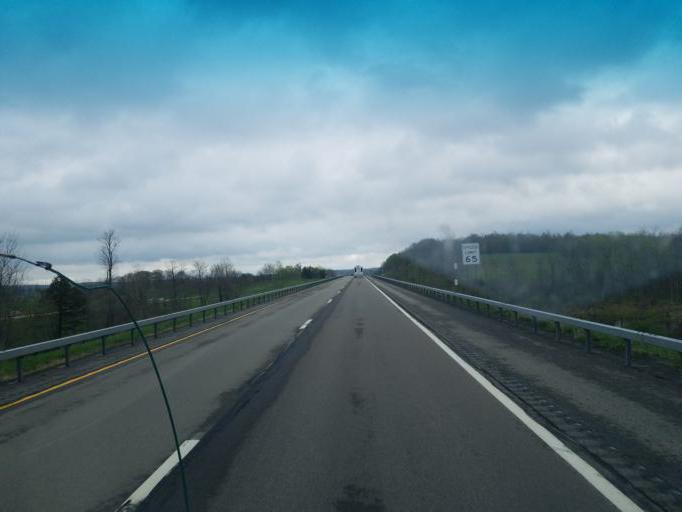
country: US
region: New York
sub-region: Chautauqua County
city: Clymer
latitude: 42.1465
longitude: -79.6315
